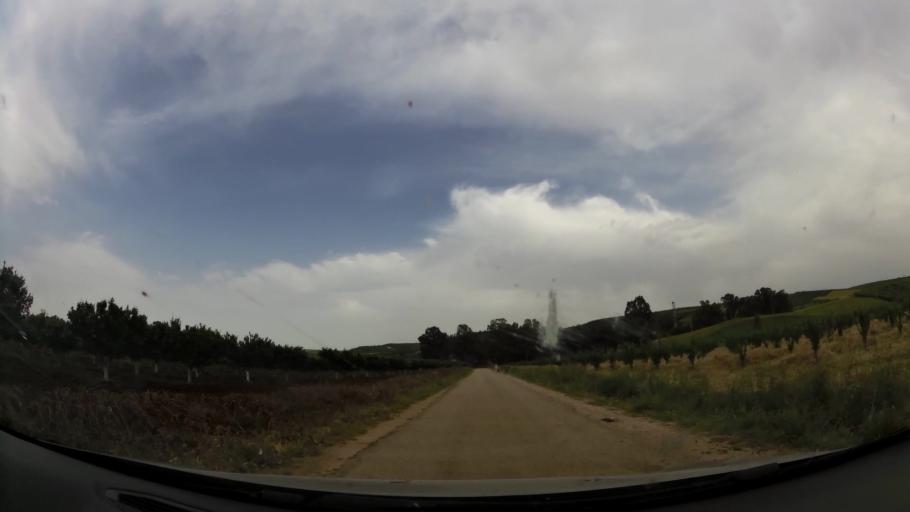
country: MA
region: Rabat-Sale-Zemmour-Zaer
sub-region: Khemisset
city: Khemisset
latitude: 33.7468
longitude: -6.2014
